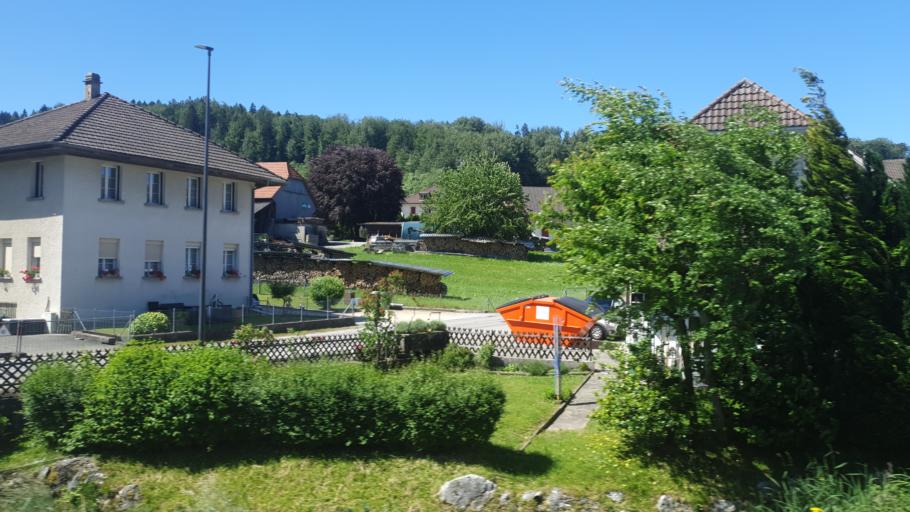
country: CH
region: Fribourg
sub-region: Sarine District
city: Belfaux
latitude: 46.8598
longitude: 7.1271
